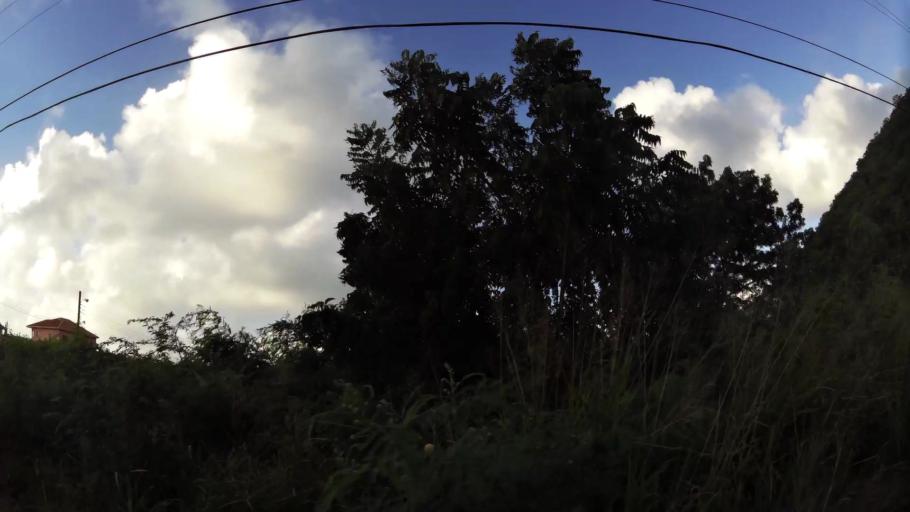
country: AG
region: Saint George
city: Piggotts
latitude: 17.1563
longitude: -61.8219
